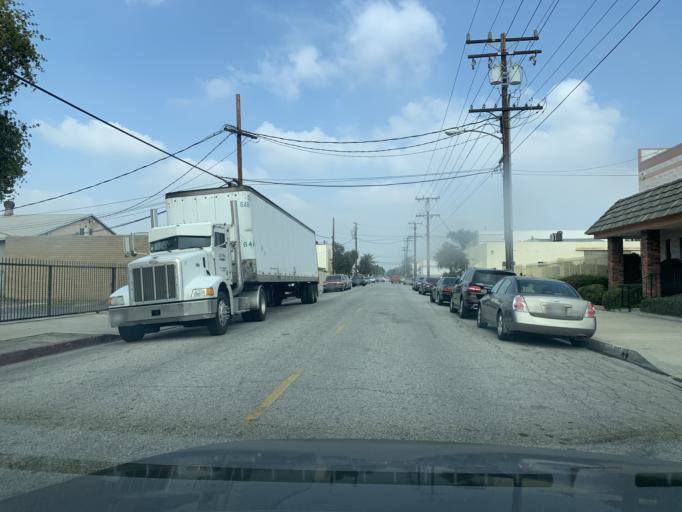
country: US
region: California
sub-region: Los Angeles County
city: South El Monte
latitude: 34.0539
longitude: -118.0528
